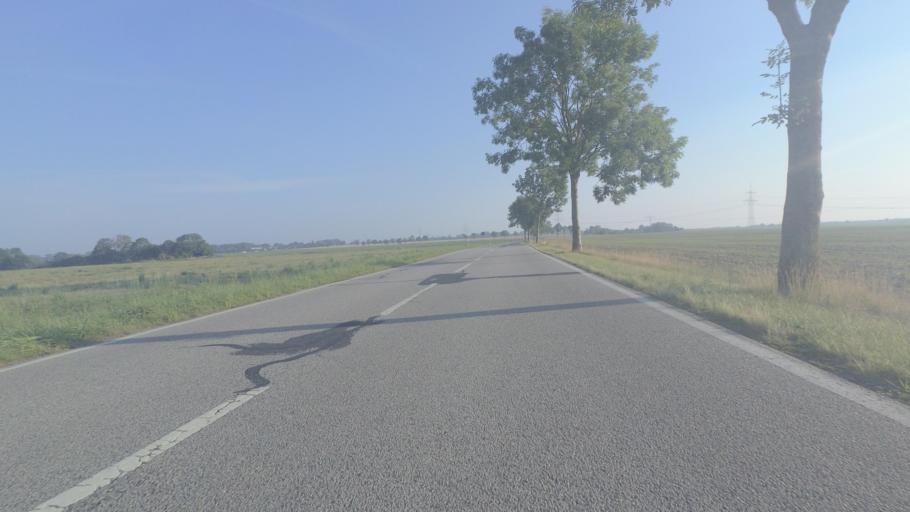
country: DE
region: Mecklenburg-Vorpommern
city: Demmin
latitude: 53.9445
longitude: 13.1178
